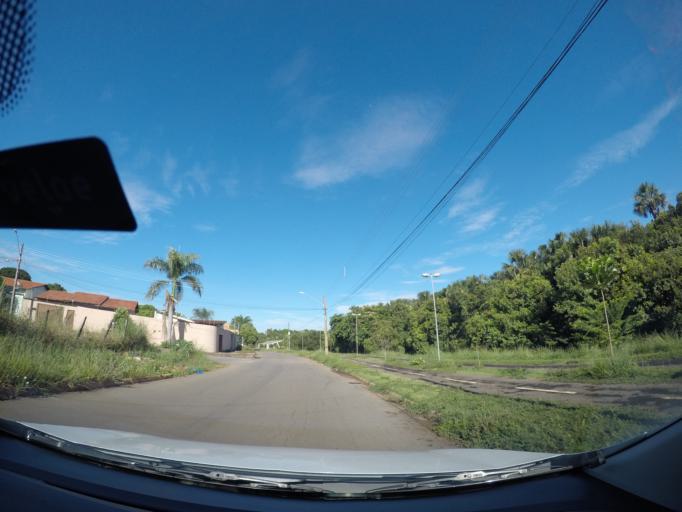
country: BR
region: Goias
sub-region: Goiania
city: Goiania
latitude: -16.7382
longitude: -49.3162
